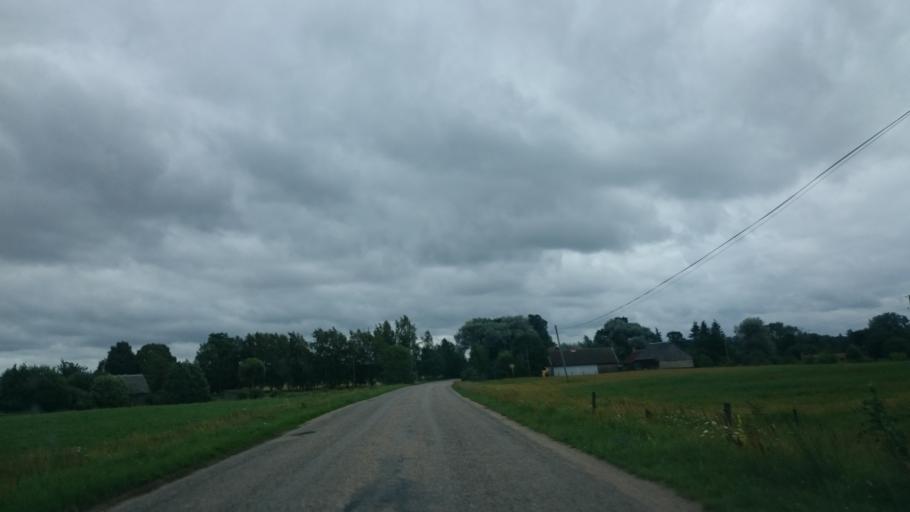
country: LV
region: Durbe
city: Liegi
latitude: 56.7430
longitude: 21.3749
